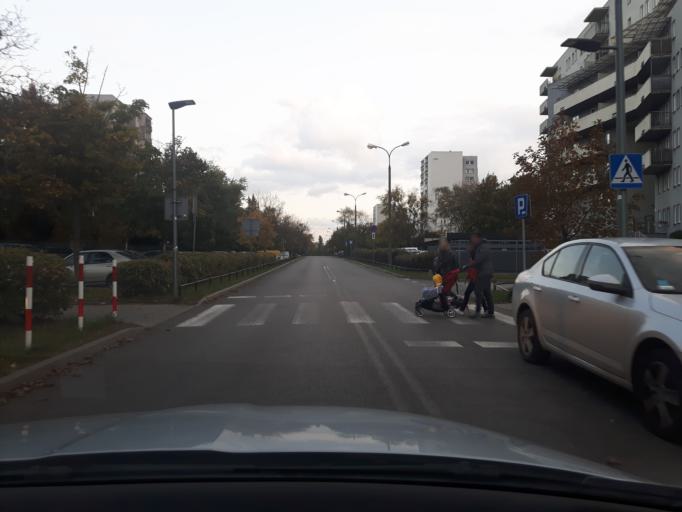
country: PL
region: Masovian Voivodeship
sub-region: Warszawa
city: Ursynow
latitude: 52.1430
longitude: 21.0497
